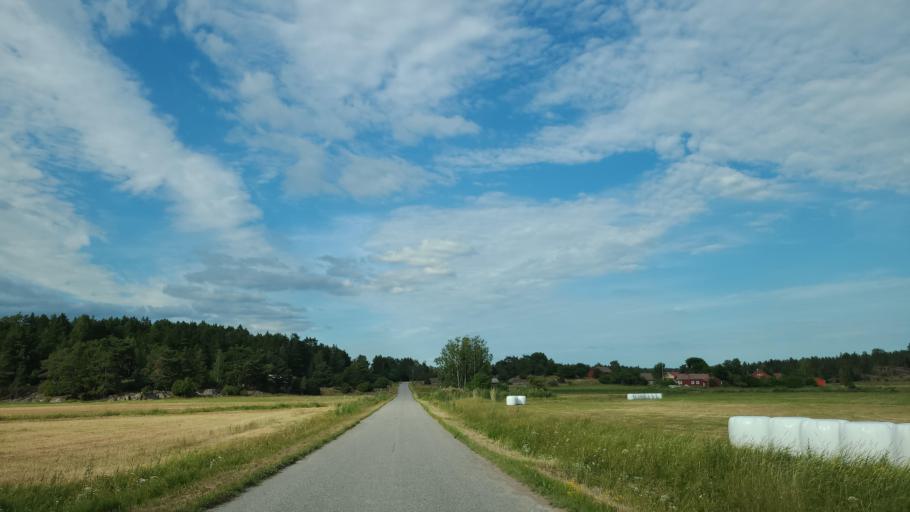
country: FI
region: Varsinais-Suomi
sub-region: Turku
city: Rymaettylae
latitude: 60.2896
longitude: 21.9317
